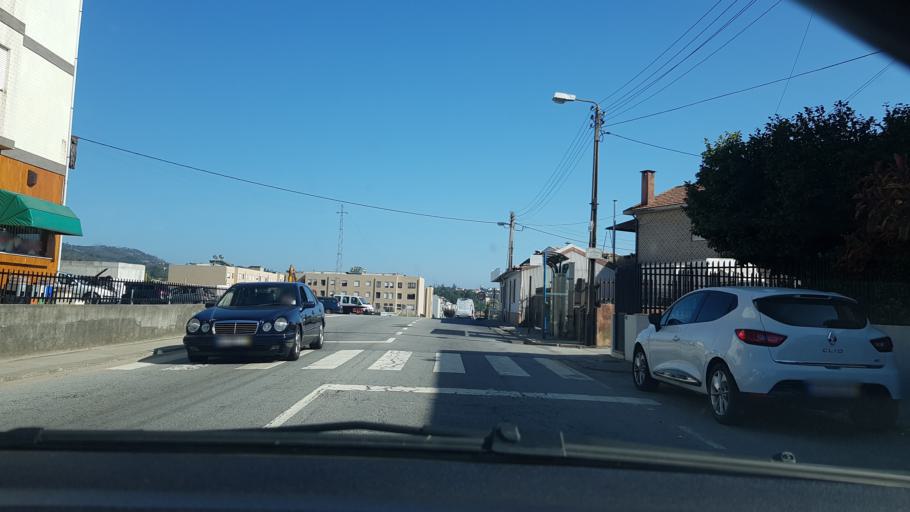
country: PT
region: Porto
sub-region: Gondomar
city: Baguim do Monte
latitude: 41.1845
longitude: -8.5396
